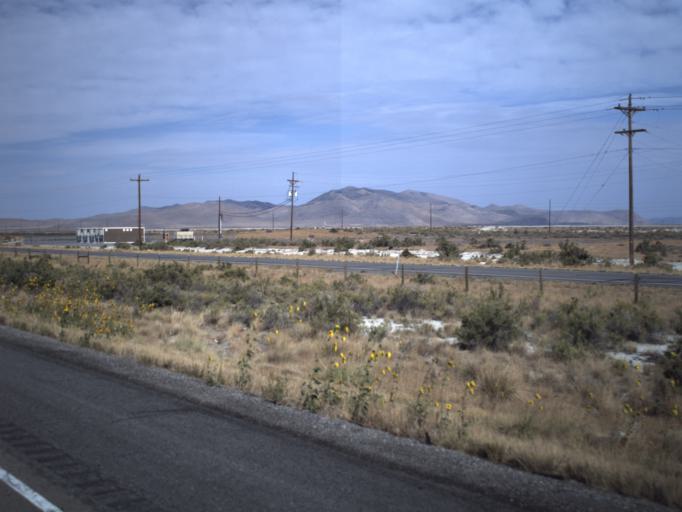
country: US
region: Utah
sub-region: Tooele County
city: Grantsville
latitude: 40.7477
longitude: -112.6688
